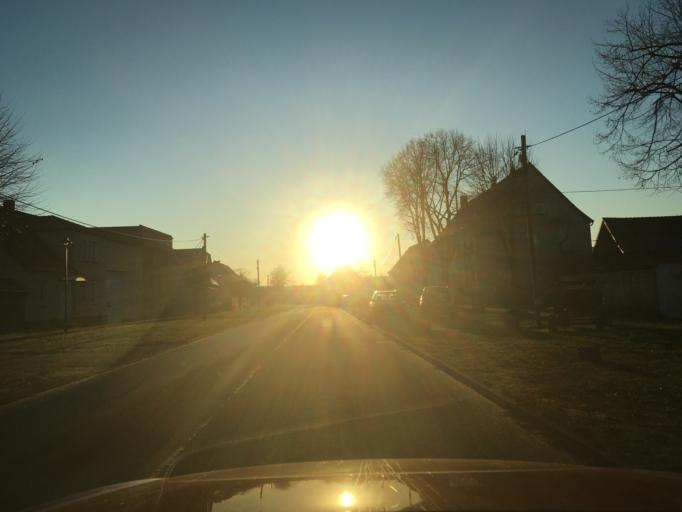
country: DE
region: Saxony-Anhalt
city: Klieken
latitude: 51.9261
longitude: 12.3253
